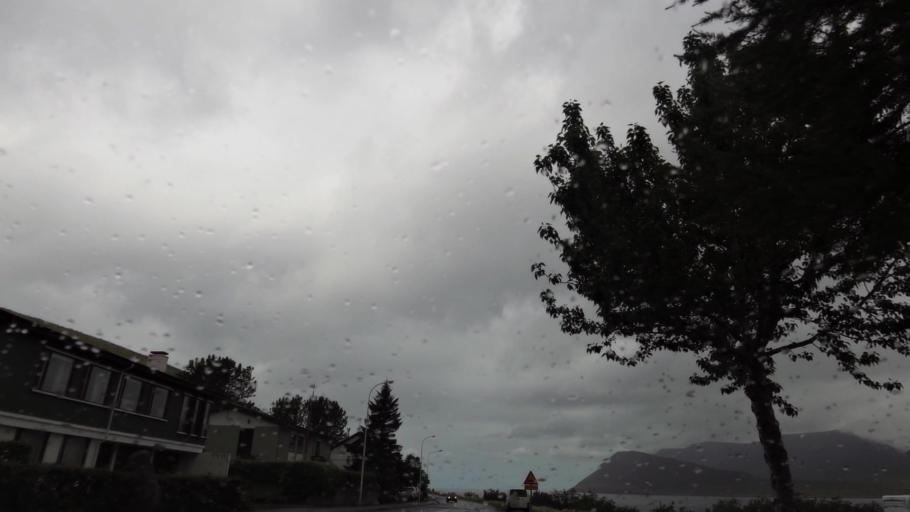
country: IS
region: Westfjords
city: Isafjoerdur
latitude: 65.8792
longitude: -23.4990
